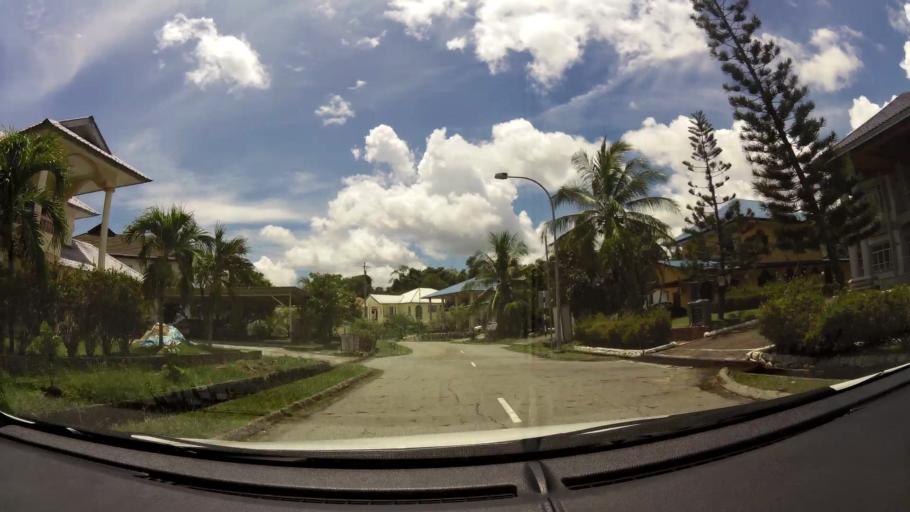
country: BN
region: Brunei and Muara
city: Bandar Seri Begawan
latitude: 4.9624
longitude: 114.9099
